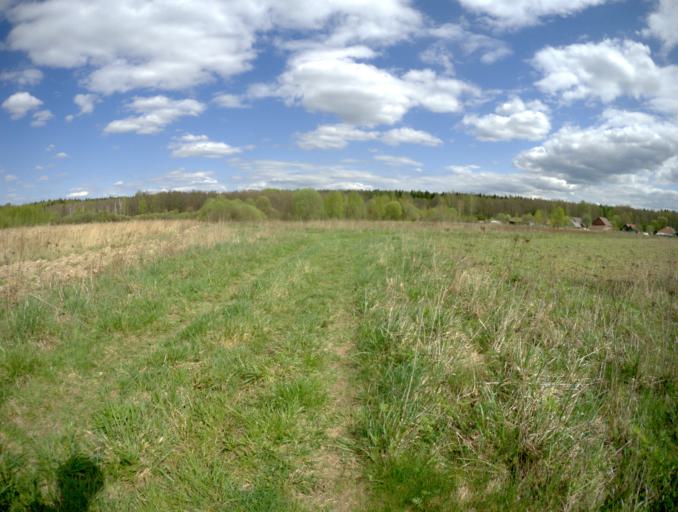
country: RU
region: Vladimir
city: Golovino
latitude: 55.9575
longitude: 40.4050
